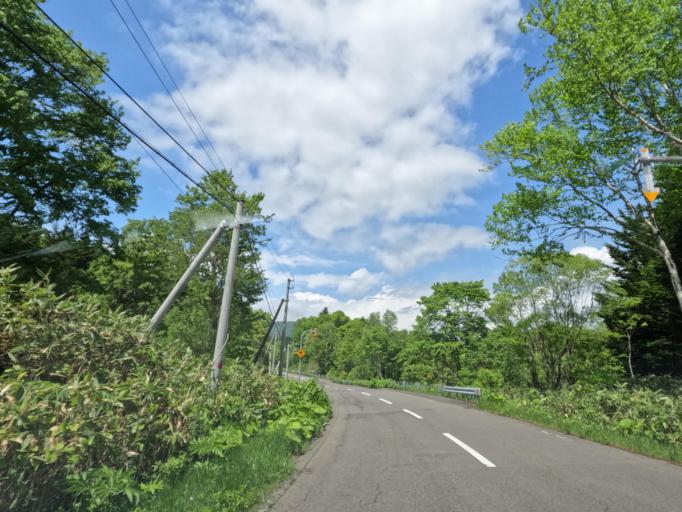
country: JP
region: Hokkaido
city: Sunagawa
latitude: 43.5111
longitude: 141.6009
